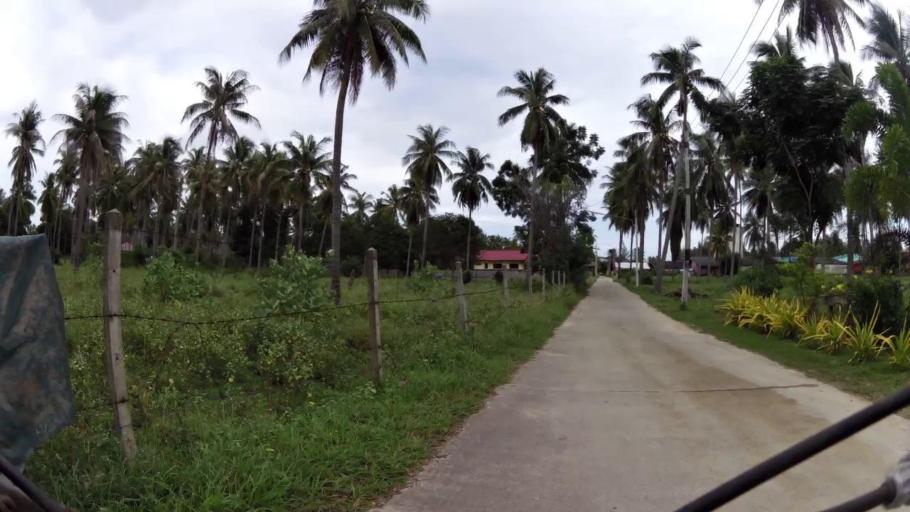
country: TH
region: Prachuap Khiri Khan
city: Prachuap Khiri Khan
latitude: 11.7387
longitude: 99.7777
